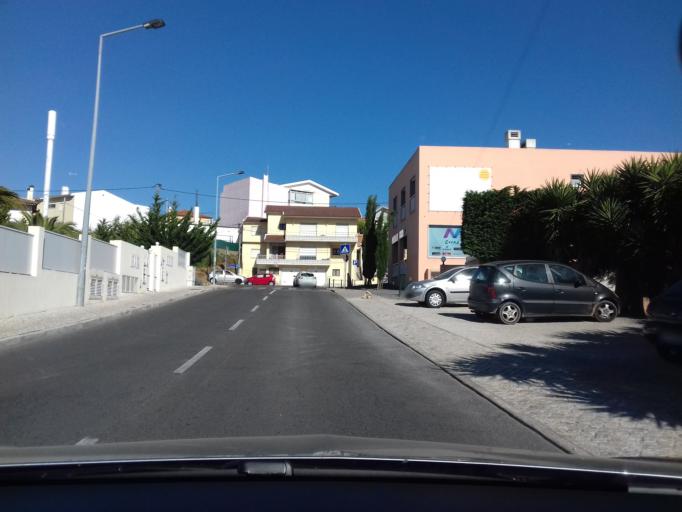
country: PT
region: Lisbon
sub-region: Cascais
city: Alcabideche
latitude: 38.7221
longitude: -9.4120
